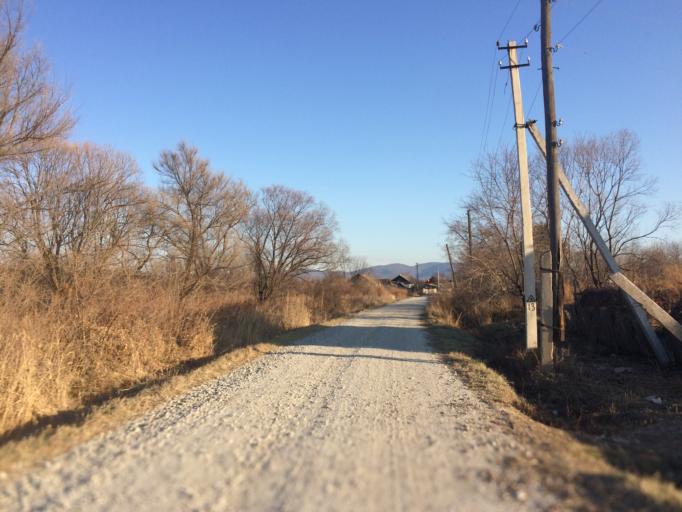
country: RU
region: Primorskiy
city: Ivanovka
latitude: 43.9557
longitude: 132.4826
